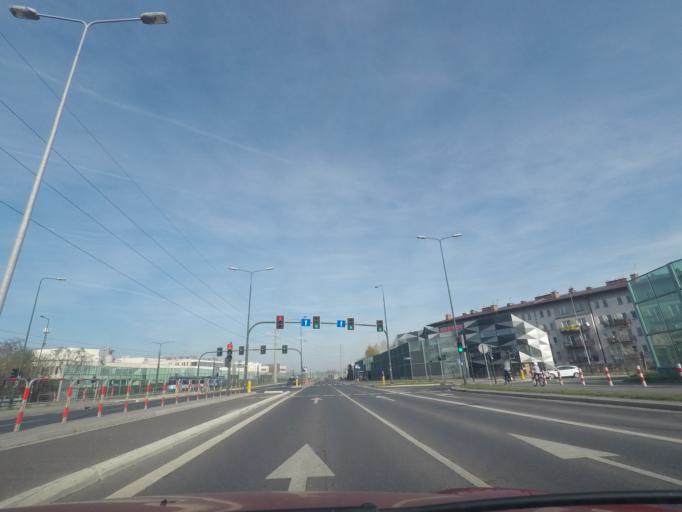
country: PL
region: Lesser Poland Voivodeship
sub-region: Krakow
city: Sidzina
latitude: 50.0239
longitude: 19.9018
